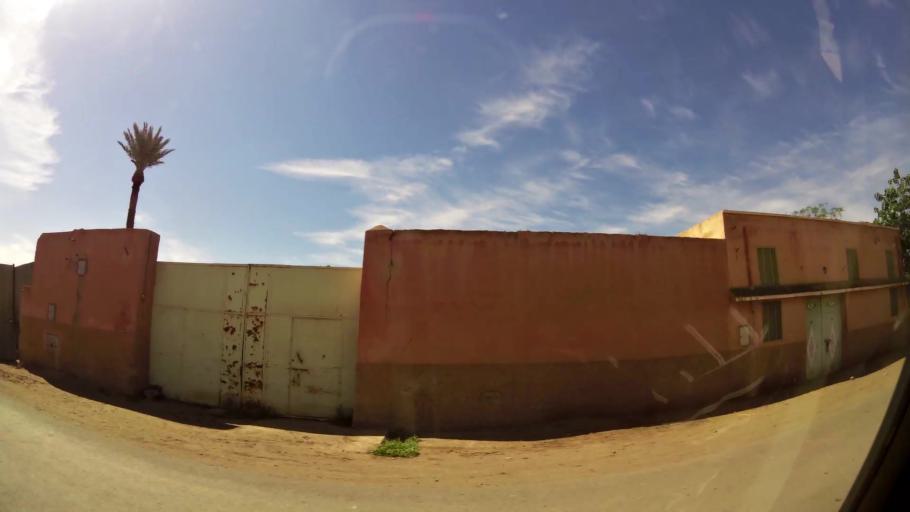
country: MA
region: Marrakech-Tensift-Al Haouz
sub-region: Marrakech
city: Marrakesh
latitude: 31.6313
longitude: -7.9564
